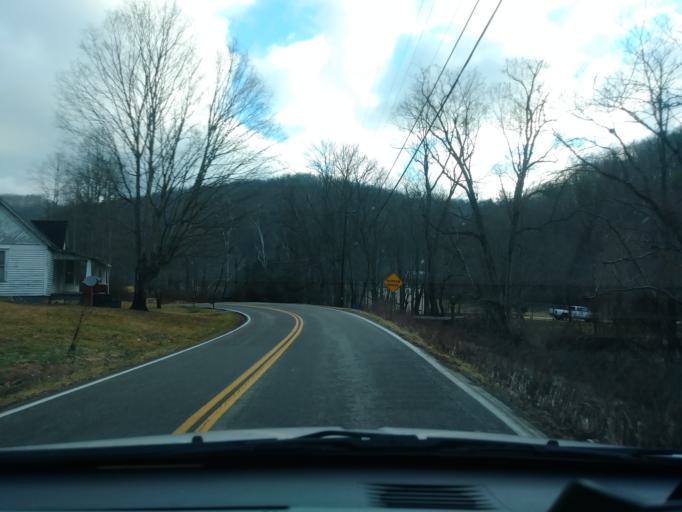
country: US
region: Tennessee
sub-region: Carter County
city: Elizabethton
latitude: 36.2271
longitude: -82.1906
